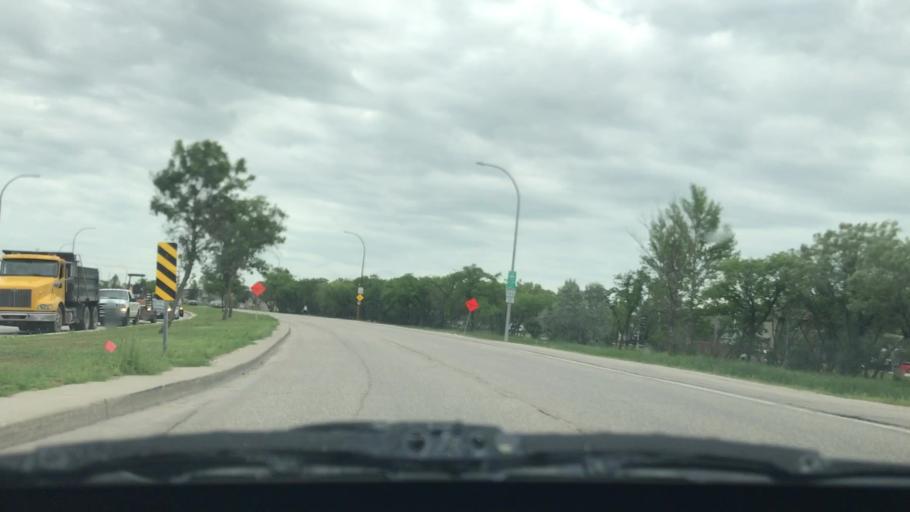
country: CA
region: Manitoba
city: Winnipeg
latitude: 49.8564
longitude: -97.0880
